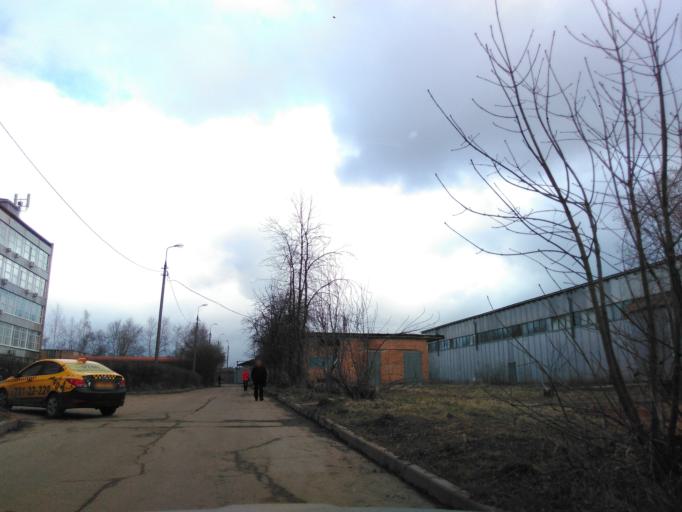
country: RU
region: Moskovskaya
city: Mendeleyevo
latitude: 56.0122
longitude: 37.2274
